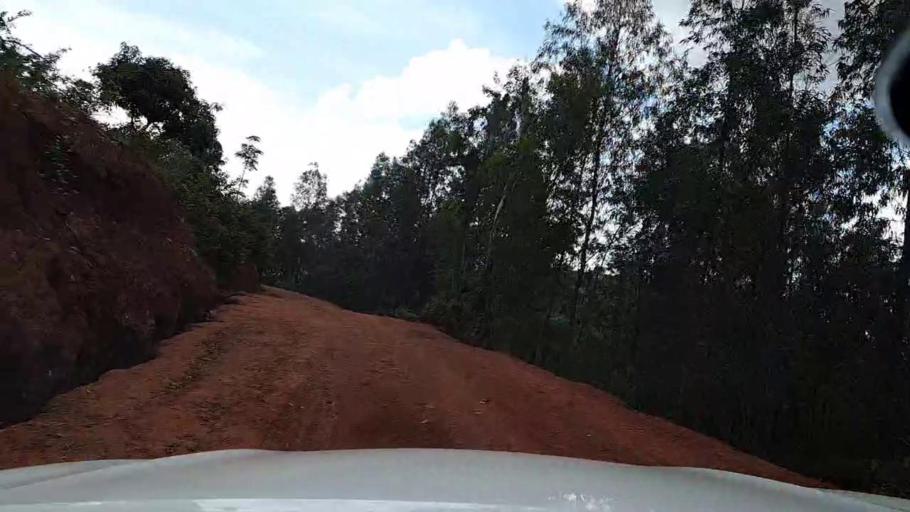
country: RW
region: Southern Province
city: Butare
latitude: -2.7446
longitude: 29.7648
